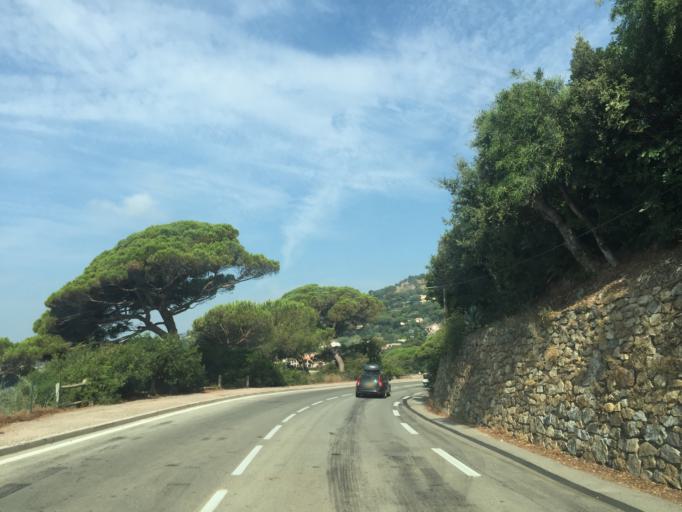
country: FR
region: Provence-Alpes-Cote d'Azur
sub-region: Departement du Var
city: Sainte-Maxime
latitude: 43.3138
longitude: 6.6636
